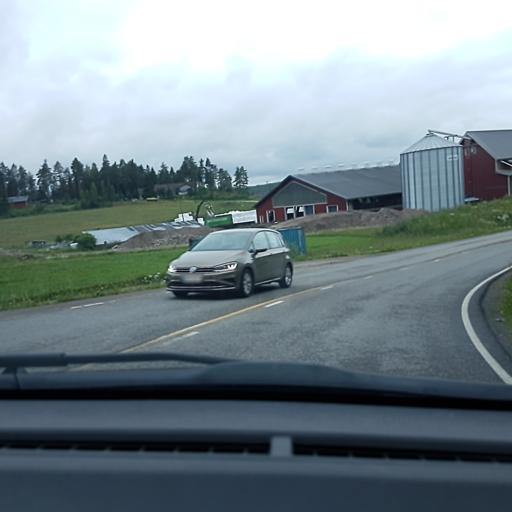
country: FI
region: Uusimaa
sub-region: Helsinki
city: Nickby
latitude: 60.4053
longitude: 25.3124
